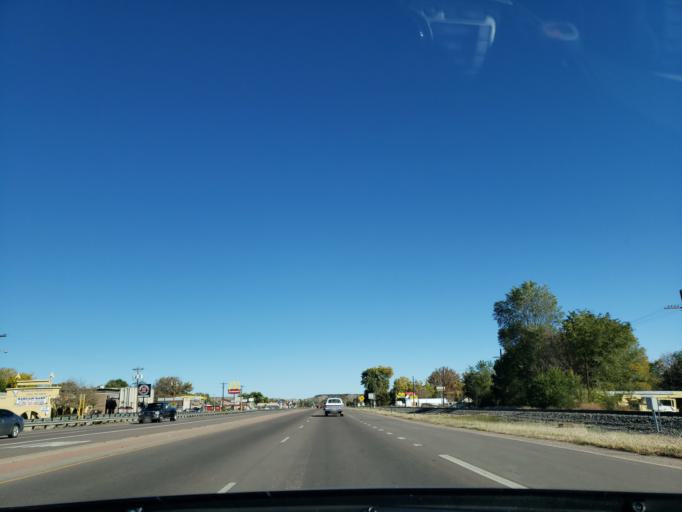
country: US
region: Colorado
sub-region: Fremont County
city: Lincoln Park
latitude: 38.4479
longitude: -105.2165
